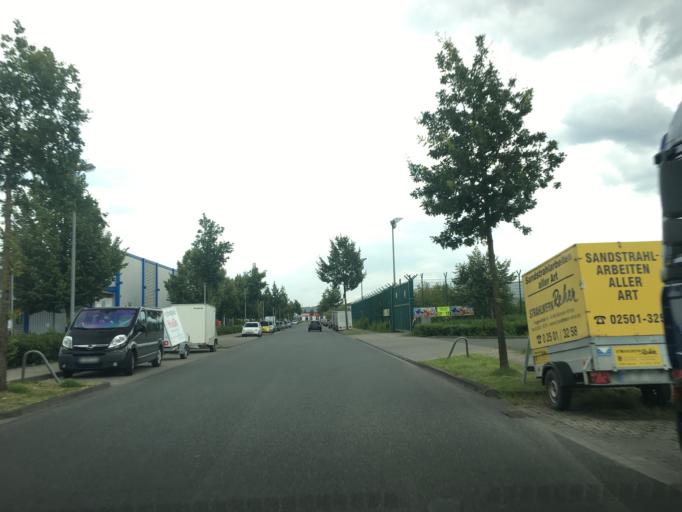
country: DE
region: North Rhine-Westphalia
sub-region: Regierungsbezirk Munster
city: Muenster
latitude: 51.9384
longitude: 7.6455
